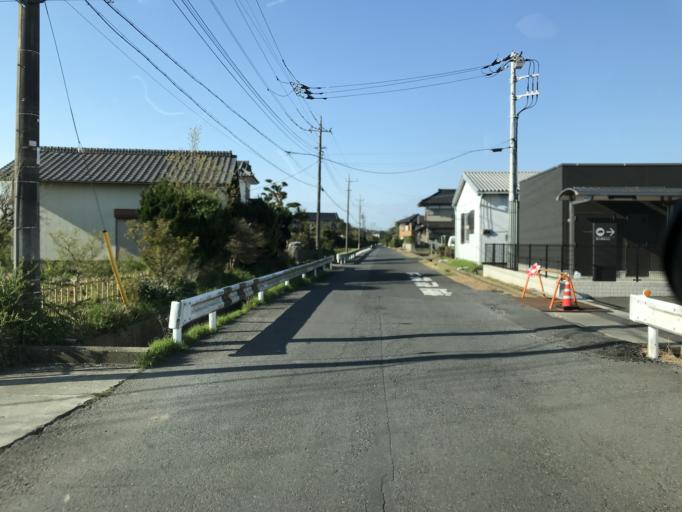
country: JP
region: Chiba
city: Omigawa
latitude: 35.8426
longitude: 140.6017
